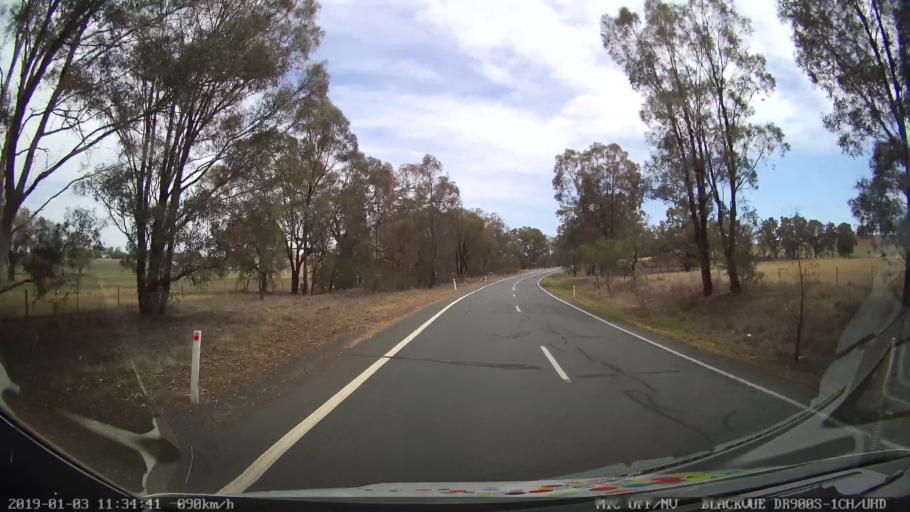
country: AU
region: New South Wales
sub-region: Weddin
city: Grenfell
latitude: -33.9321
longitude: 148.1612
